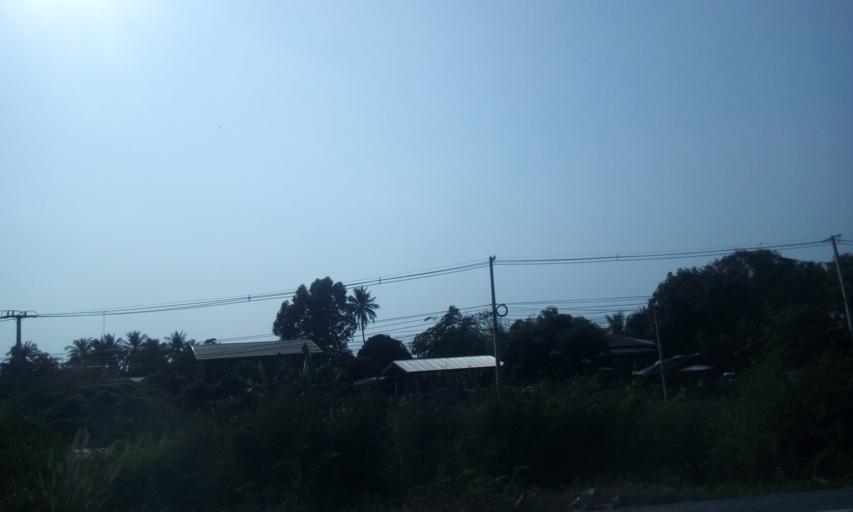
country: TH
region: Ang Thong
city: Chaiyo
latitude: 14.7197
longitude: 100.4581
